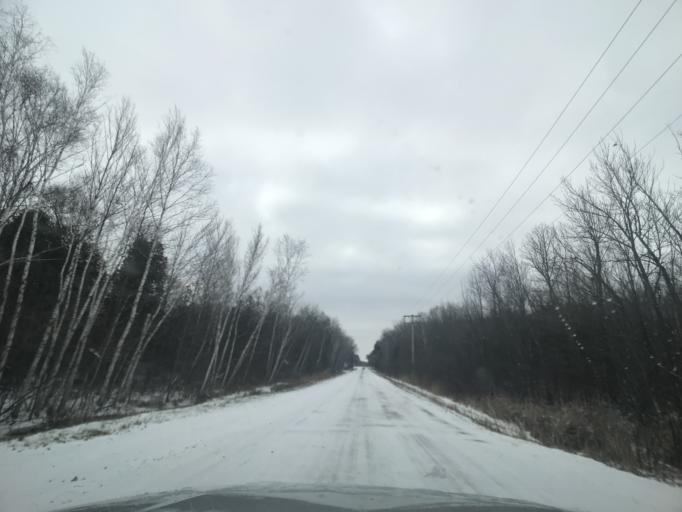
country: US
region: Wisconsin
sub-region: Brown County
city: Suamico
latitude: 44.7054
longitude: -88.1012
